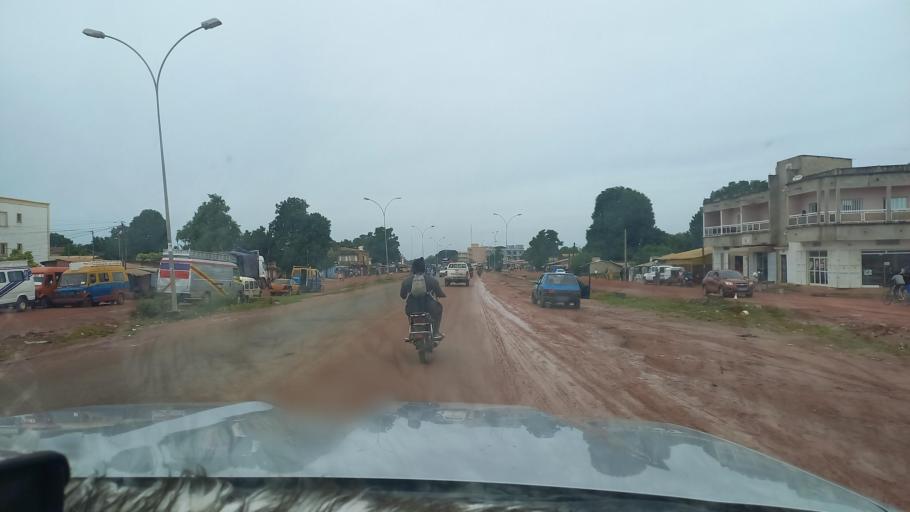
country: SN
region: Ziguinchor
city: Ziguinchor
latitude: 12.5632
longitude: -16.2668
